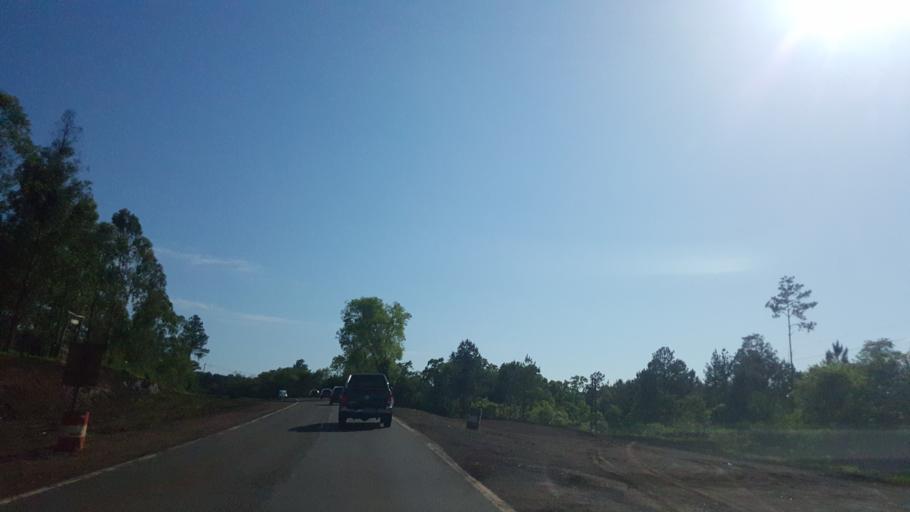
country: AR
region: Misiones
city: Santa Ana
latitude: -27.3675
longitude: -55.5604
